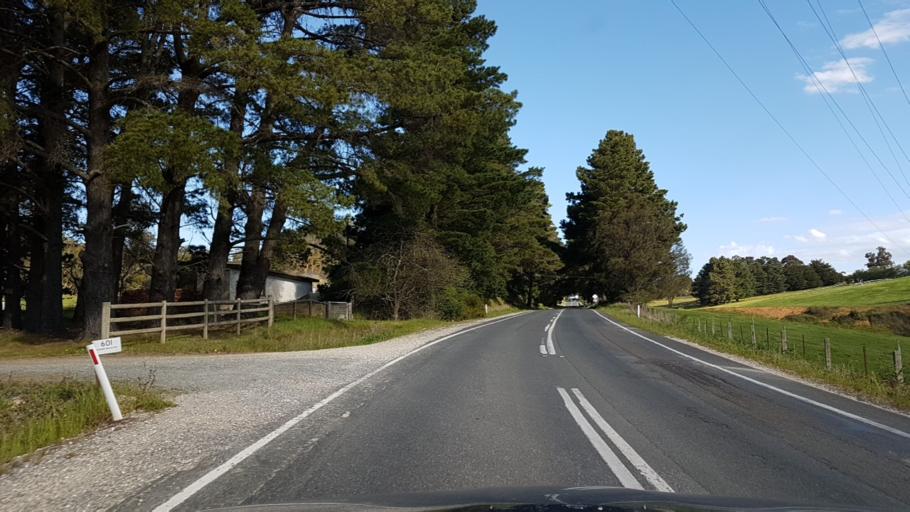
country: AU
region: South Australia
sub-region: Adelaide Hills
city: Lobethal
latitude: -34.8728
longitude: 138.8893
